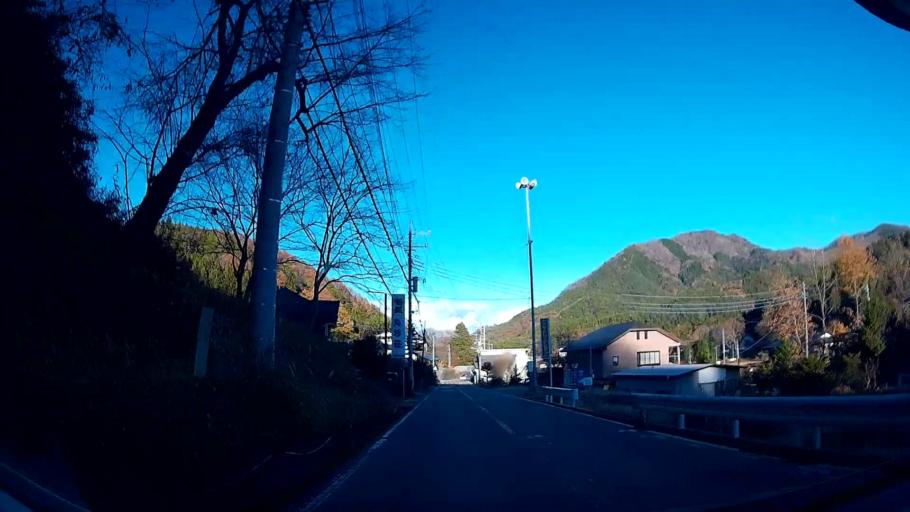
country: JP
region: Yamanashi
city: Otsuki
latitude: 35.4969
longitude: 138.9825
